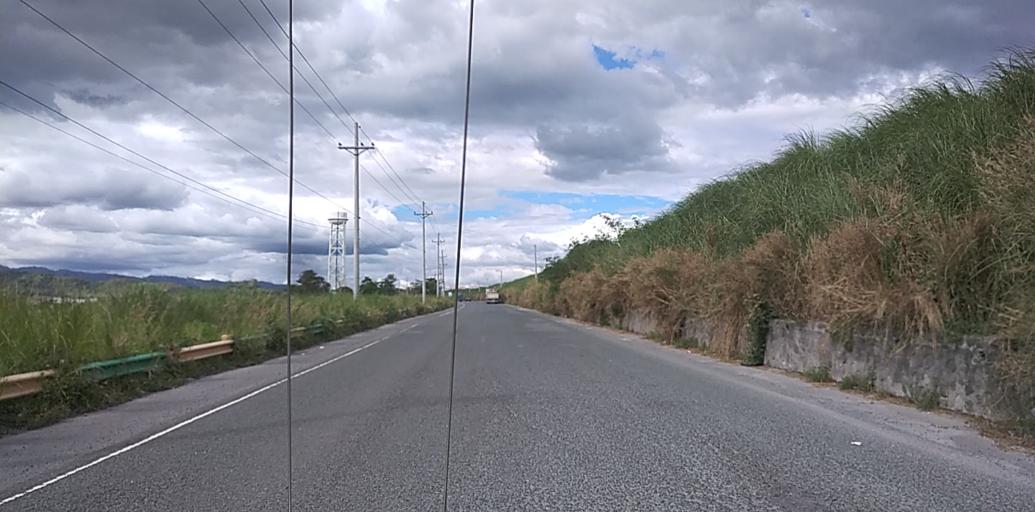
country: PH
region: Central Luzon
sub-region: Province of Pampanga
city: Dolores
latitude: 15.1092
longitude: 120.5191
